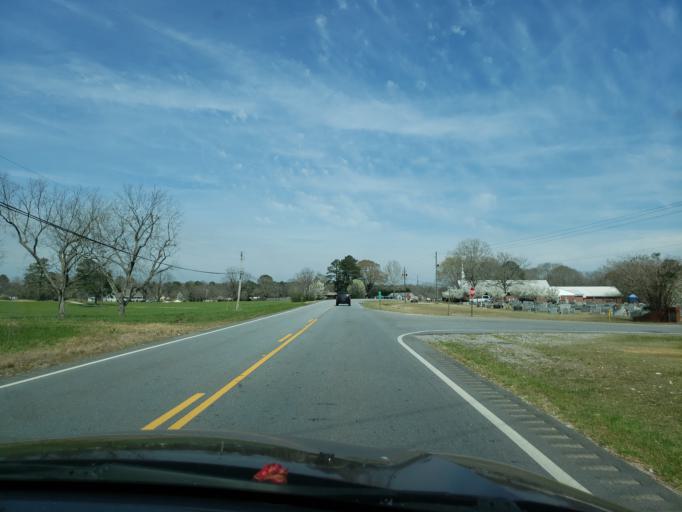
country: US
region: Alabama
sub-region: Elmore County
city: Tallassee
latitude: 32.5556
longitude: -85.8287
